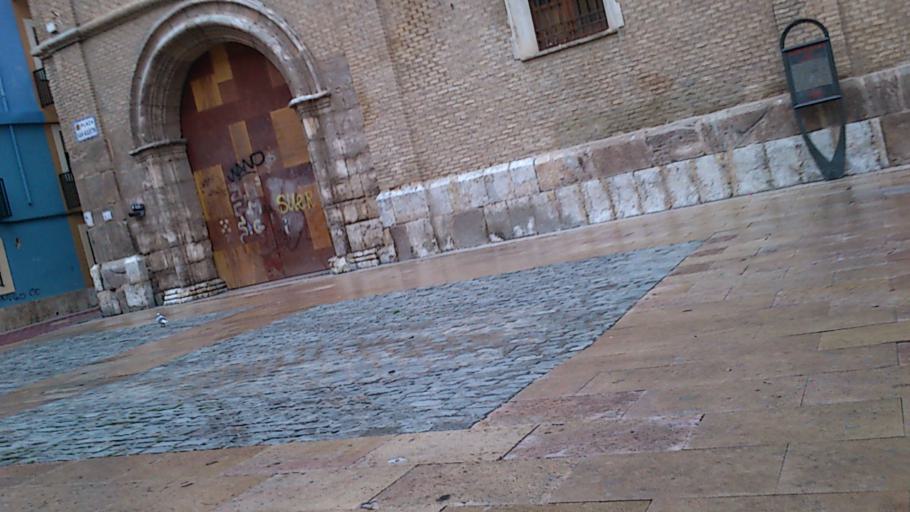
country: ES
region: Aragon
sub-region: Provincia de Zaragoza
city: Zaragoza
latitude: 41.6508
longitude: -0.8711
